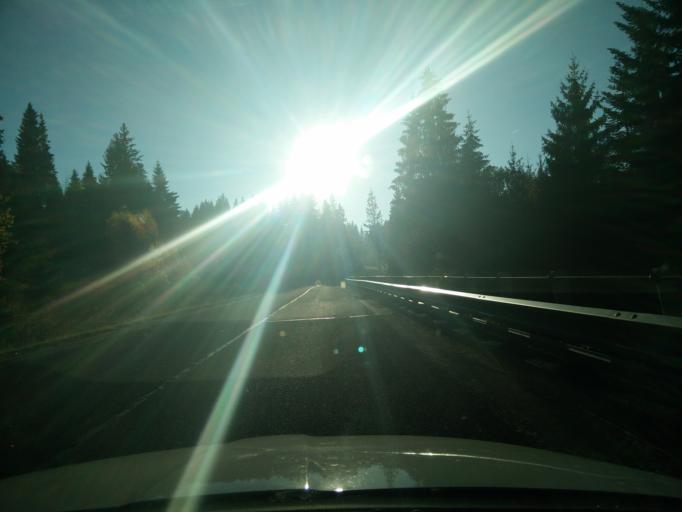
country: SK
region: Zilinsky
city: Oravska Lesna
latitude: 49.3707
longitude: 19.1285
